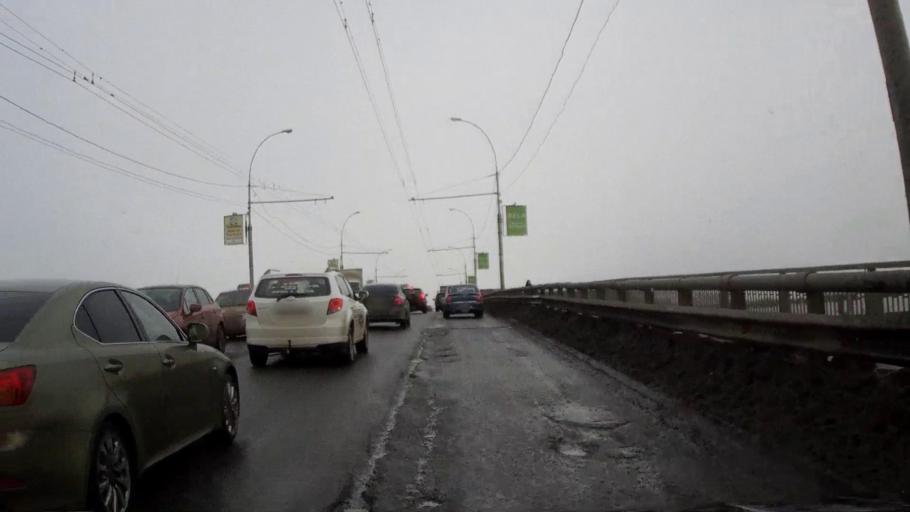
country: RU
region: Vologda
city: Vologda
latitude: 59.2157
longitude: 39.8601
